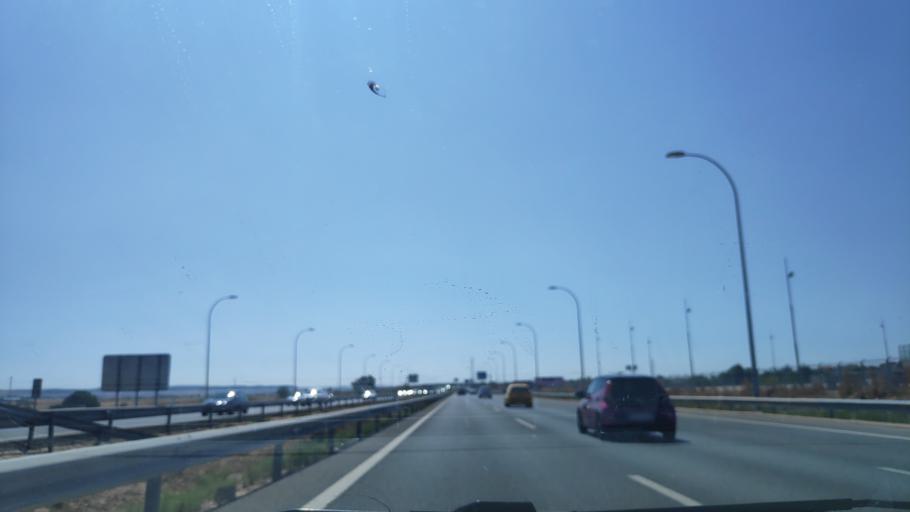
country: ES
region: Madrid
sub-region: Provincia de Madrid
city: Torrejon de la Calzada
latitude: 40.2068
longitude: -3.7908
